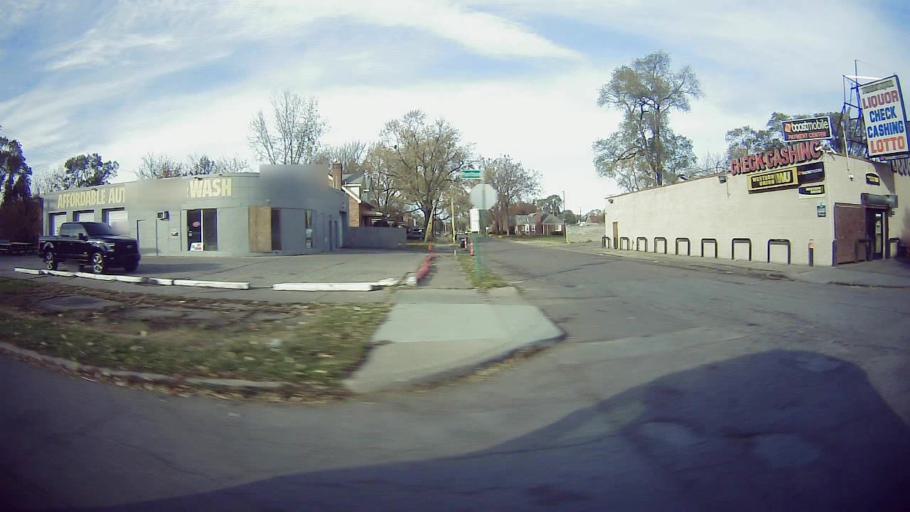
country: US
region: Michigan
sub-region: Oakland County
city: Oak Park
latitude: 42.4087
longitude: -83.2056
